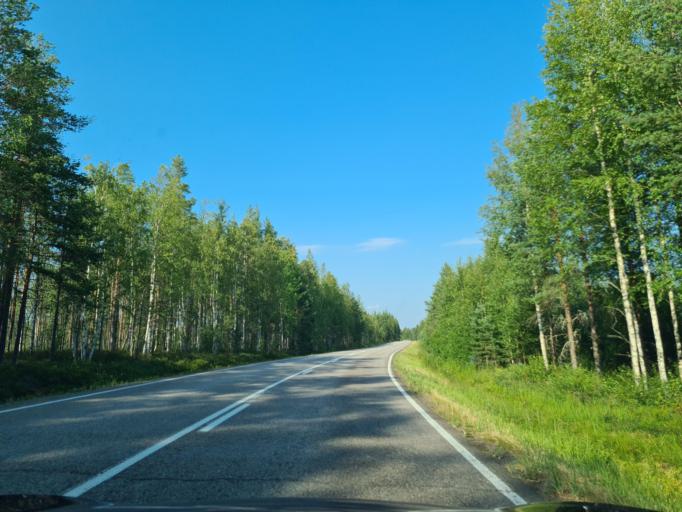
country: FI
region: Satakunta
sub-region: Pohjois-Satakunta
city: Karvia
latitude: 62.3157
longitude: 22.6587
